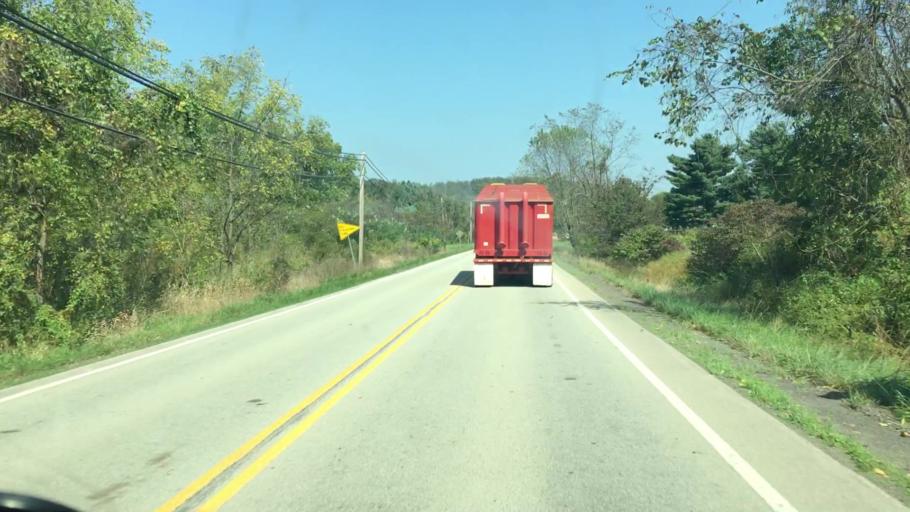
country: US
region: Pennsylvania
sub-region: Washington County
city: Washington
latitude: 40.1289
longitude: -80.2863
